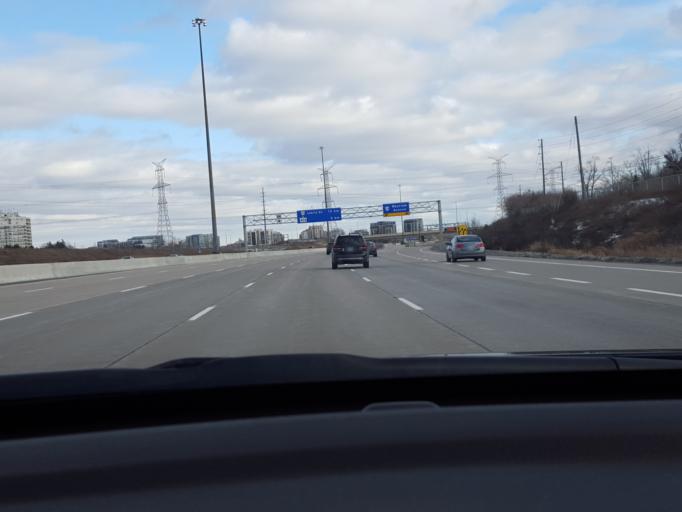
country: CA
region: Ontario
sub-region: York
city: Richmond Hill
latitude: 43.8385
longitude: -79.4143
